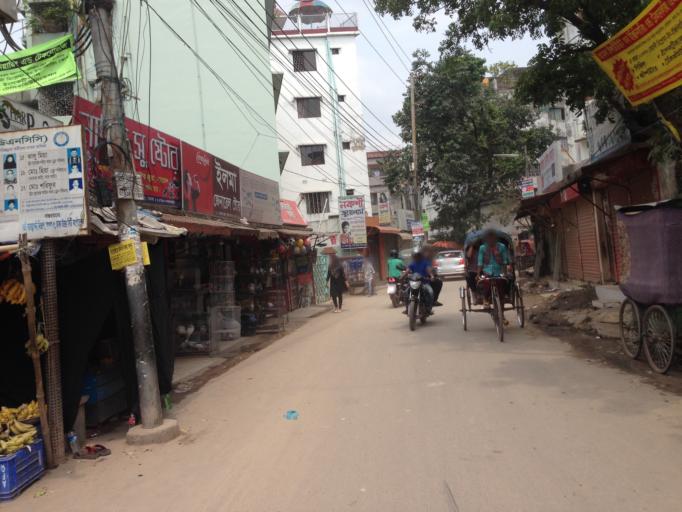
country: BD
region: Dhaka
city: Paltan
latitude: 23.7619
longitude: 90.4169
